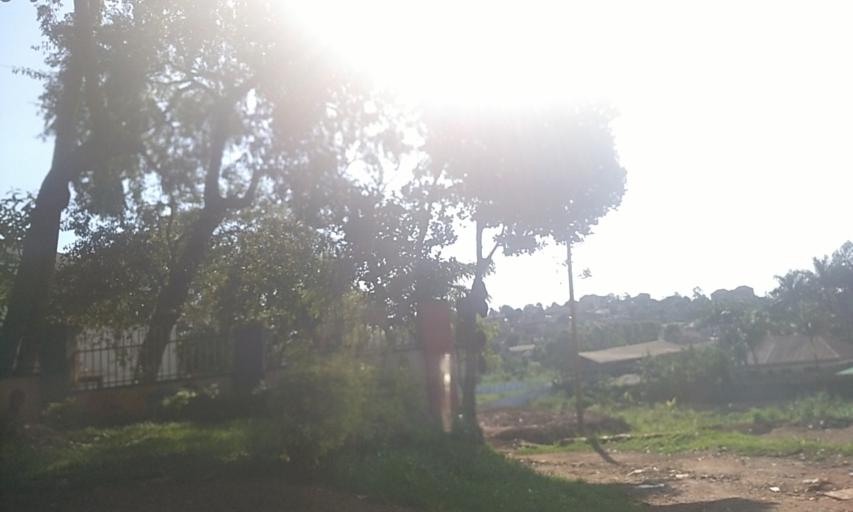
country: UG
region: Central Region
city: Kampala Central Division
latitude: 0.3159
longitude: 32.5532
